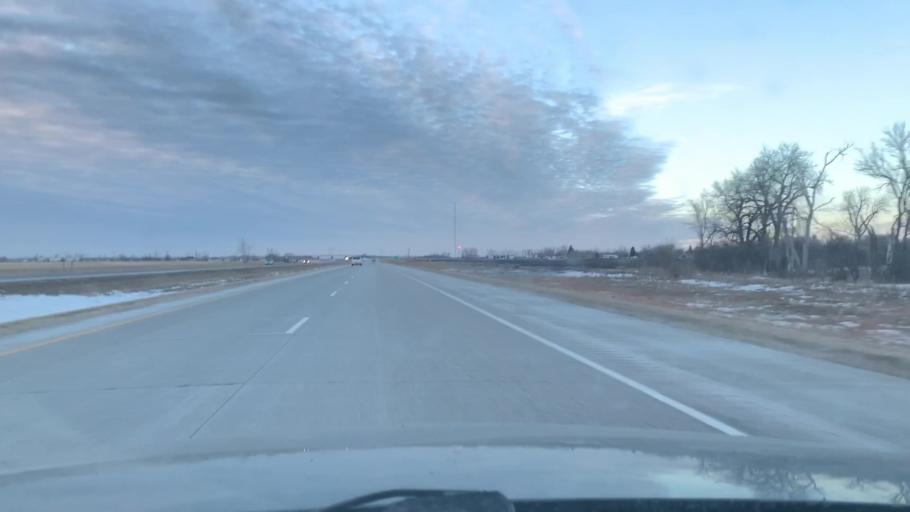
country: US
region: North Dakota
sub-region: Barnes County
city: Valley City
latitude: 46.9117
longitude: -97.6713
